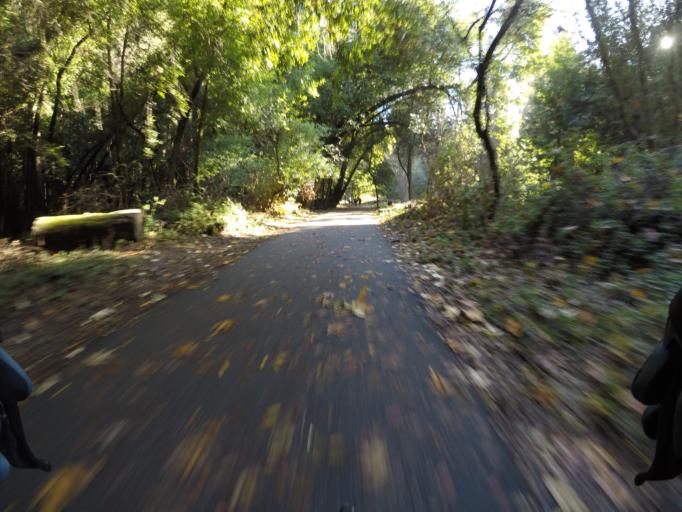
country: US
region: California
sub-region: Santa Cruz County
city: Mount Hermon
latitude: 37.0368
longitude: -122.0622
